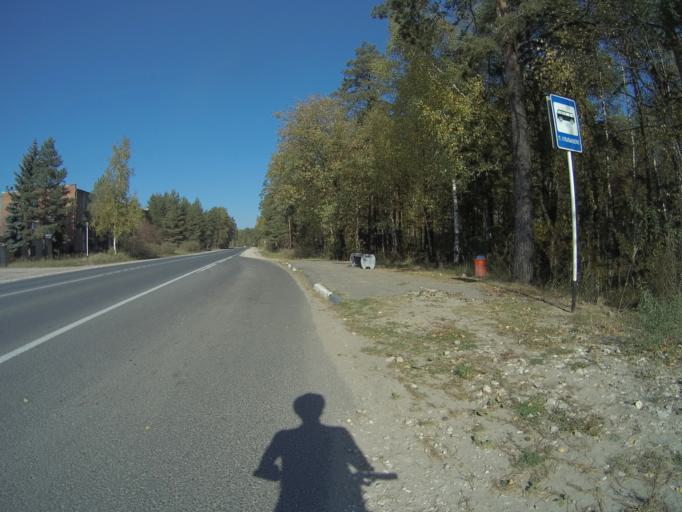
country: RU
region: Vladimir
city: Raduzhnyy
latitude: 56.0256
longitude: 40.3808
